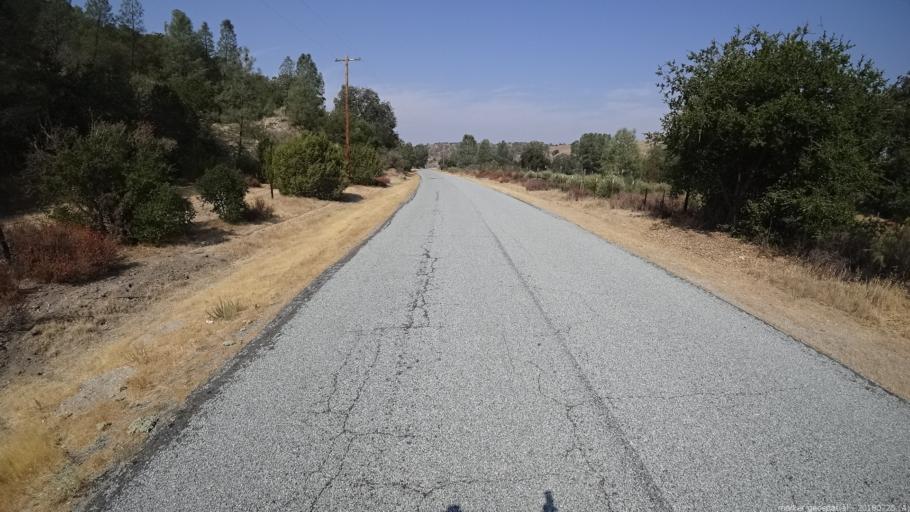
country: US
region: California
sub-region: San Luis Obispo County
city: San Miguel
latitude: 35.8563
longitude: -120.5968
